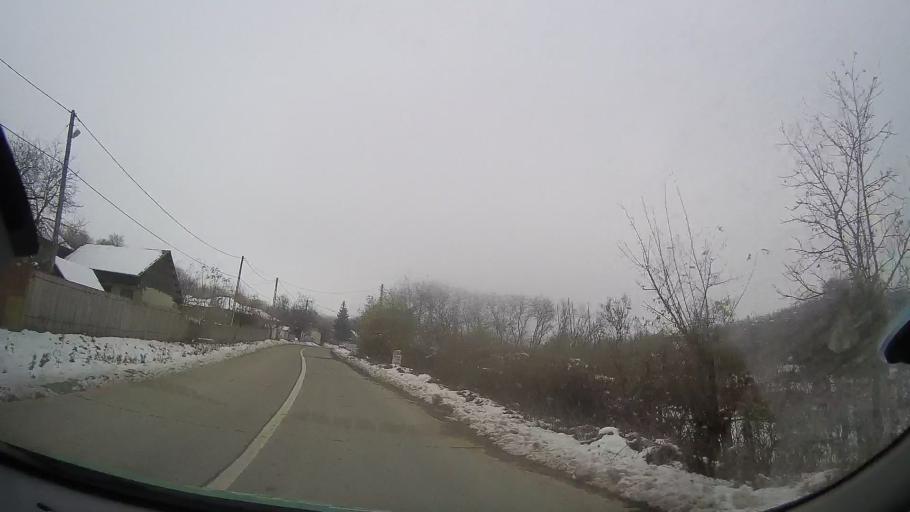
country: RO
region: Vrancea
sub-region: Comuna Boghesti
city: Boghesti
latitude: 46.2001
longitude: 27.4431
